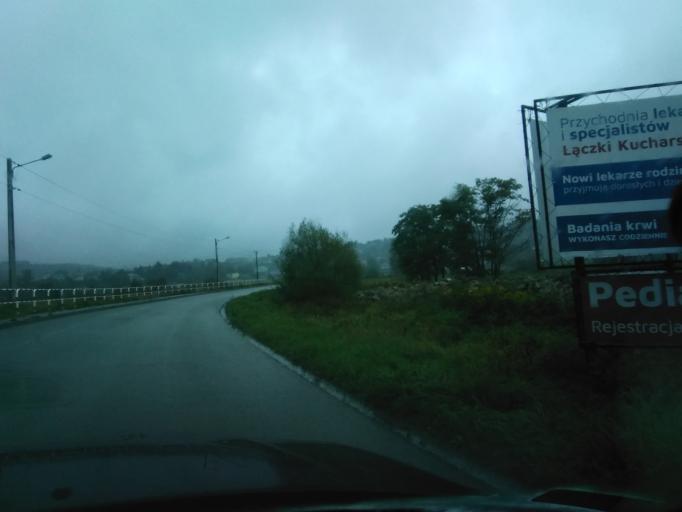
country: PL
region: Subcarpathian Voivodeship
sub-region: Powiat ropczycko-sedziszowski
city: Niedzwiada
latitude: 49.9955
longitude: 21.5559
